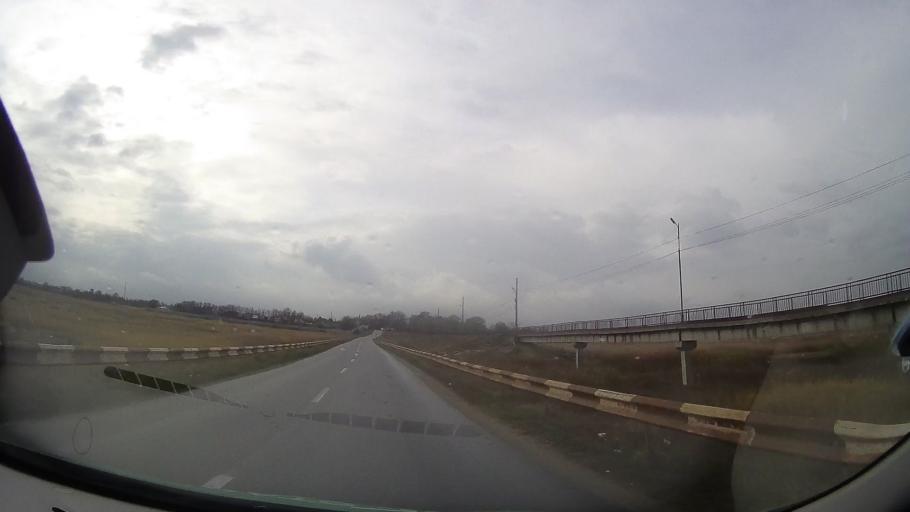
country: RO
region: Ialomita
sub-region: Comuna Fierbinti-Targ
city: Fierbintii de Jos
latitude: 44.6879
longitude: 26.3910
